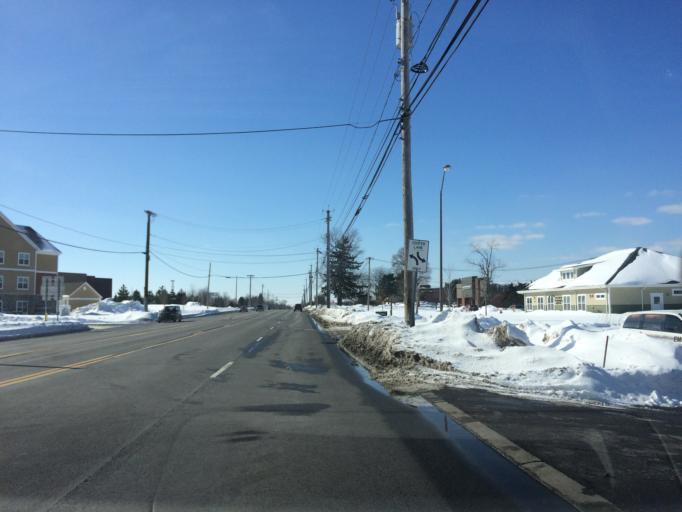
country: US
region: New York
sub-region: Monroe County
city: Rochester
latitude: 43.0948
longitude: -77.6141
